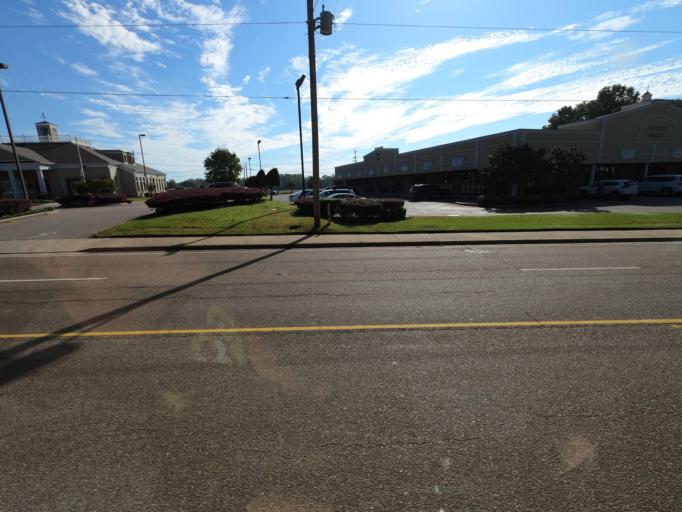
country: US
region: Tennessee
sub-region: Shelby County
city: Millington
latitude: 35.3549
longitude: -89.8964
